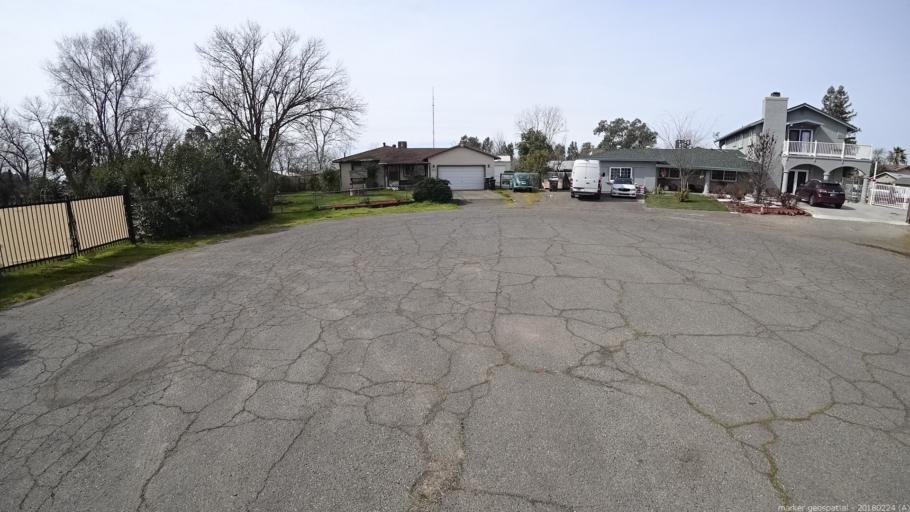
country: US
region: California
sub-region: Sacramento County
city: Elverta
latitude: 38.7090
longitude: -121.4694
